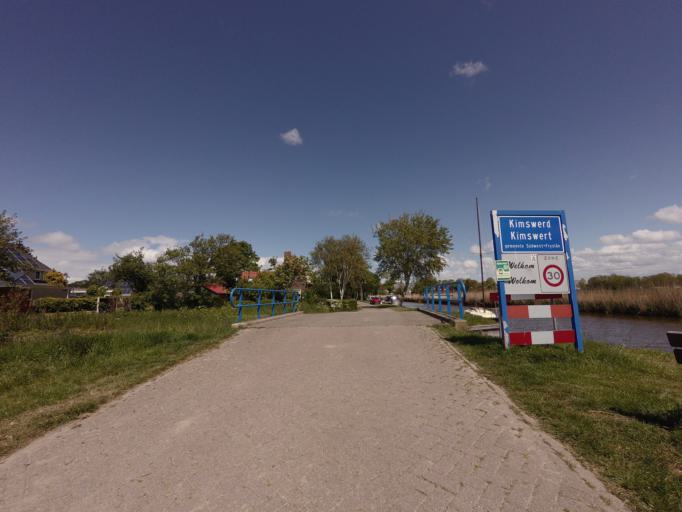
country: NL
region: Friesland
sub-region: Gemeente Harlingen
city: Harlingen
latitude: 53.1388
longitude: 5.4362
